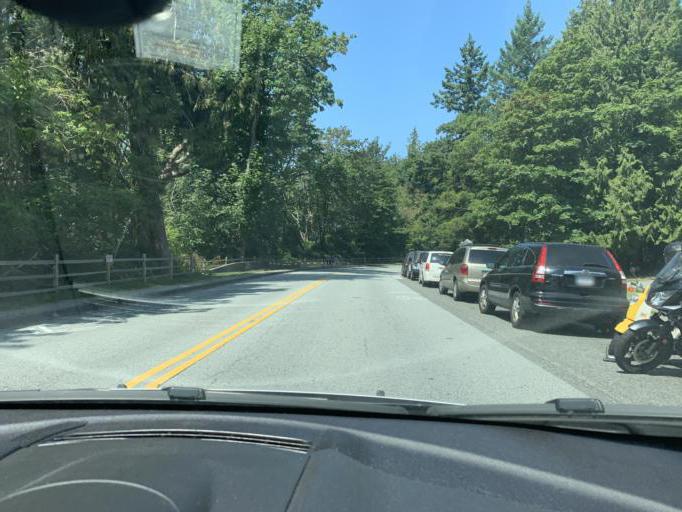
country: CA
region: British Columbia
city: West End
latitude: 49.2637
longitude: -123.2598
